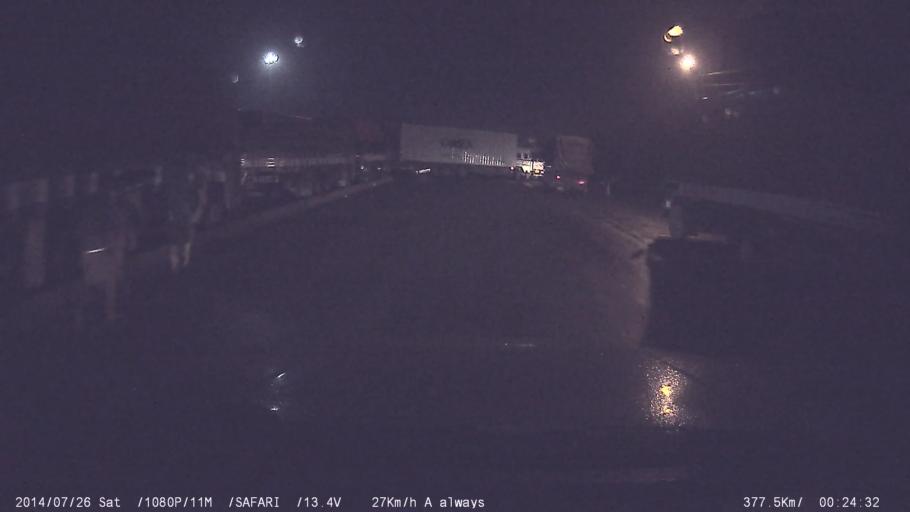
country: IN
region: Tamil Nadu
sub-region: Coimbatore
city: Madukkarai
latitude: 10.8366
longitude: 76.8374
